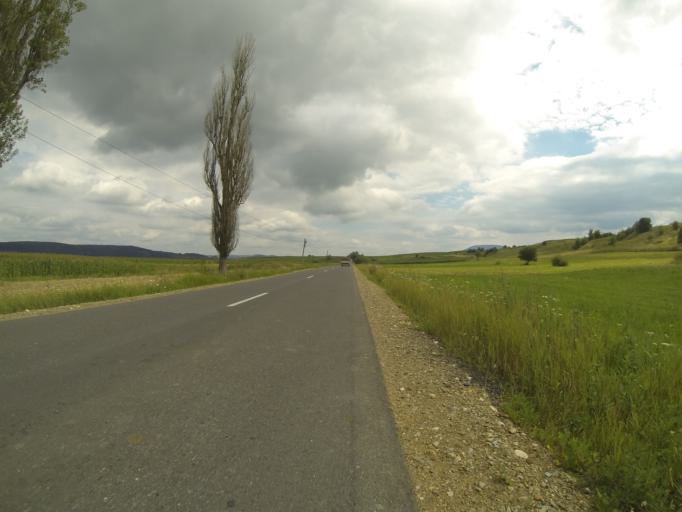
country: RO
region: Brasov
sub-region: Comuna Parau
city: Parau
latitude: 45.8632
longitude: 25.2000
